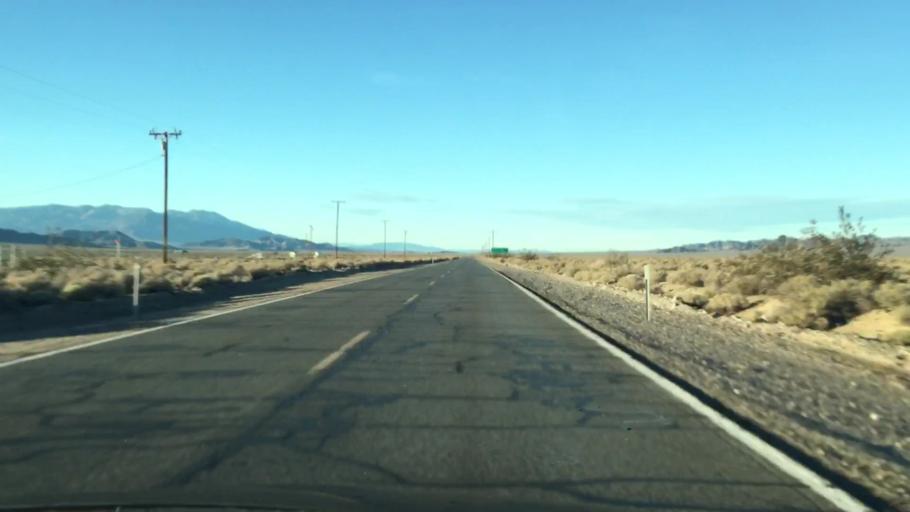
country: US
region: California
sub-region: San Bernardino County
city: Fort Irwin
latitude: 35.2848
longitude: -116.0785
